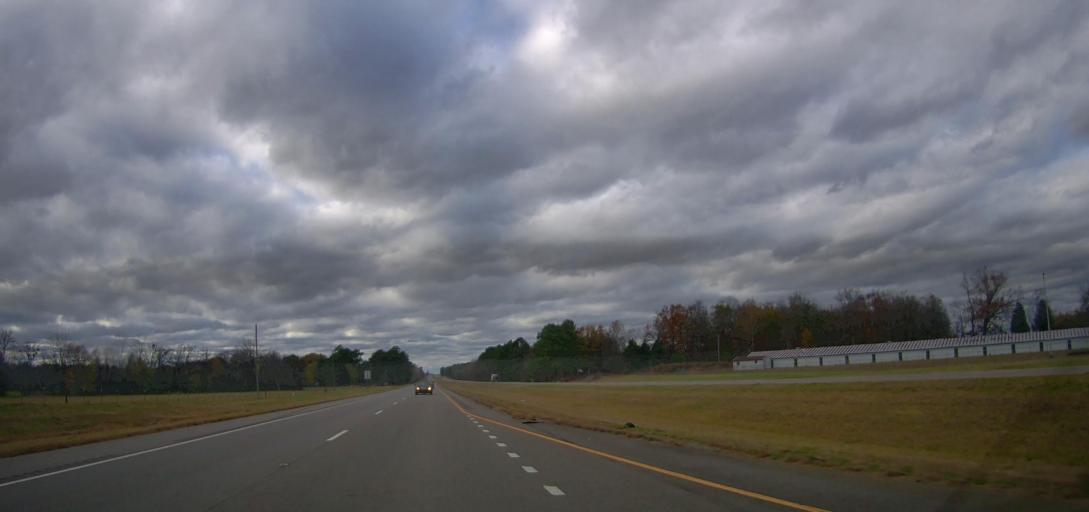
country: US
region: Alabama
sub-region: Morgan County
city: Danville
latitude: 34.3451
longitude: -87.0344
